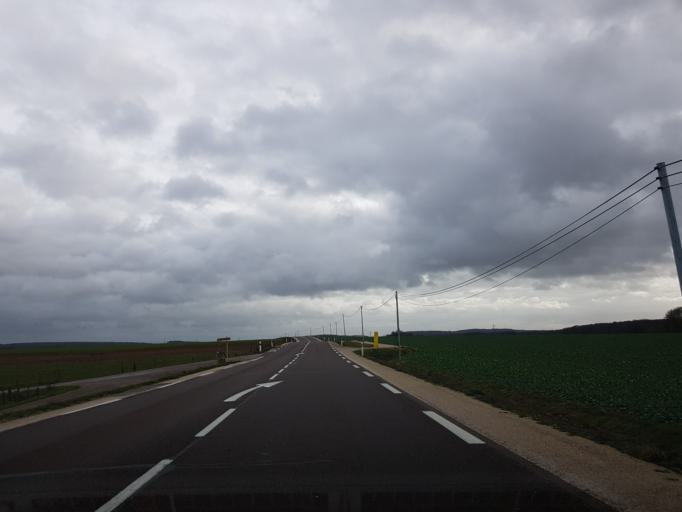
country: FR
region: Champagne-Ardenne
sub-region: Departement de la Haute-Marne
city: Fayl-Billot
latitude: 47.7658
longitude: 5.7096
